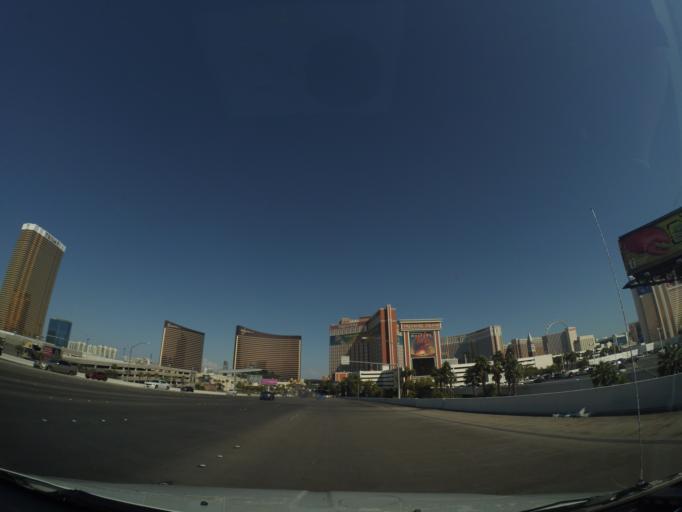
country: US
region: Nevada
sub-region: Clark County
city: Paradise
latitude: 36.1259
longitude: -115.1770
